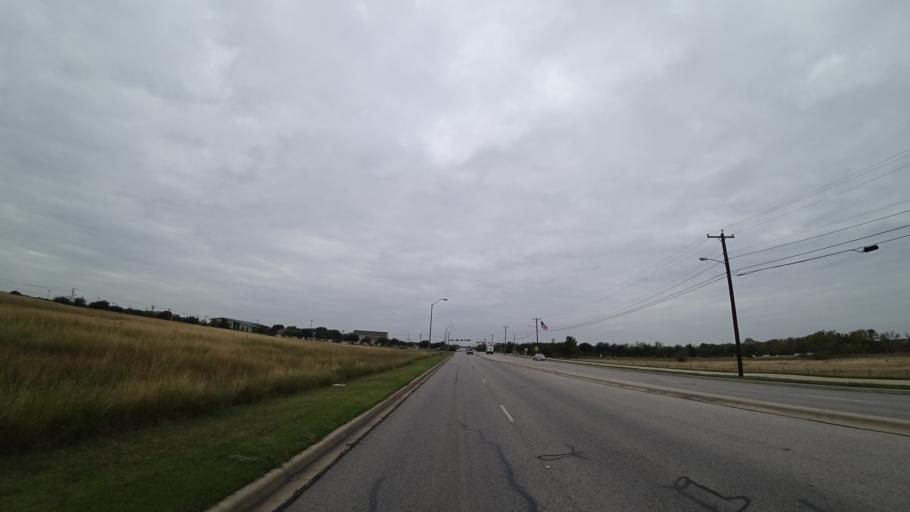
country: US
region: Texas
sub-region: Travis County
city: Pflugerville
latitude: 30.4582
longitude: -97.6144
